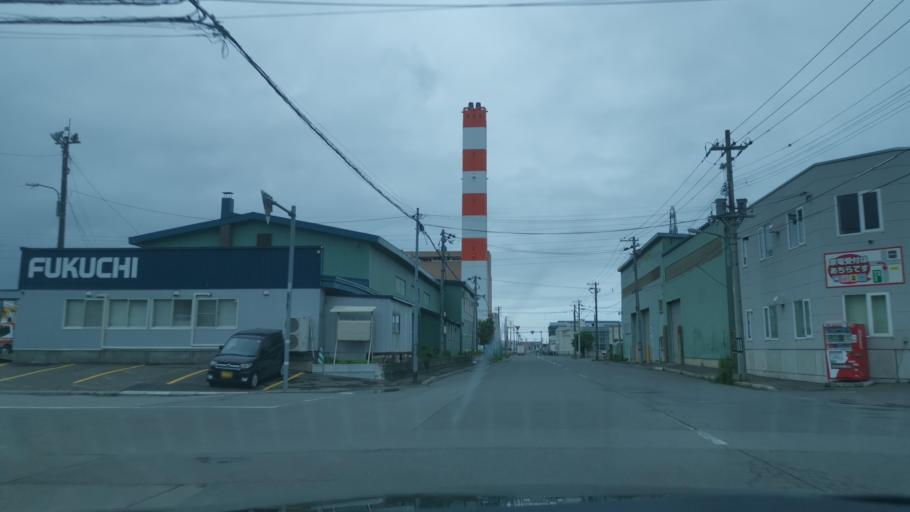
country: JP
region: Hokkaido
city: Sapporo
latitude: 43.1080
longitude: 141.2857
